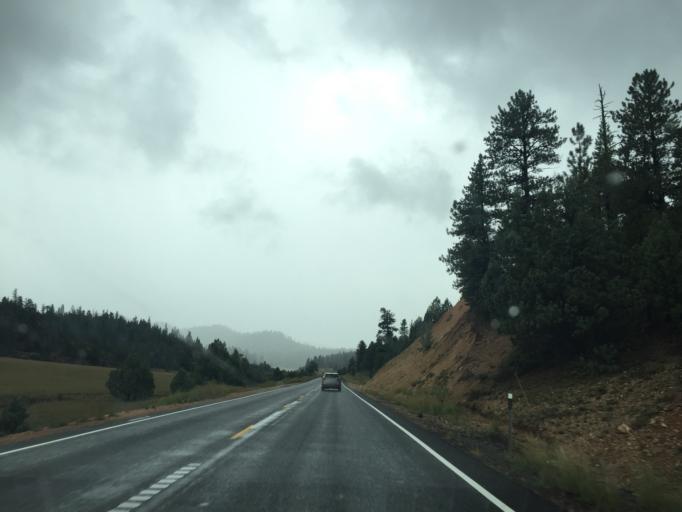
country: US
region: Utah
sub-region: Kane County
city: Kanab
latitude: 37.4372
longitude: -112.5383
